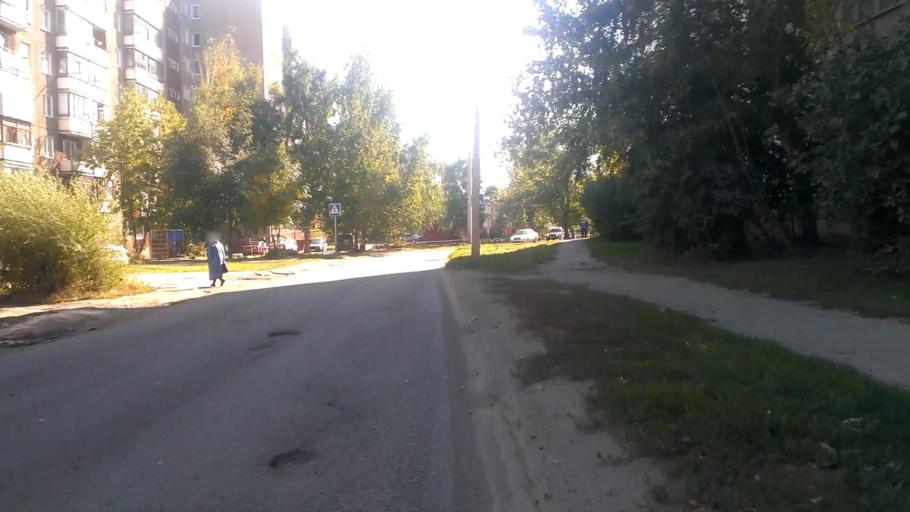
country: RU
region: Altai Krai
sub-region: Gorod Barnaulskiy
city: Barnaul
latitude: 53.3728
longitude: 83.6912
